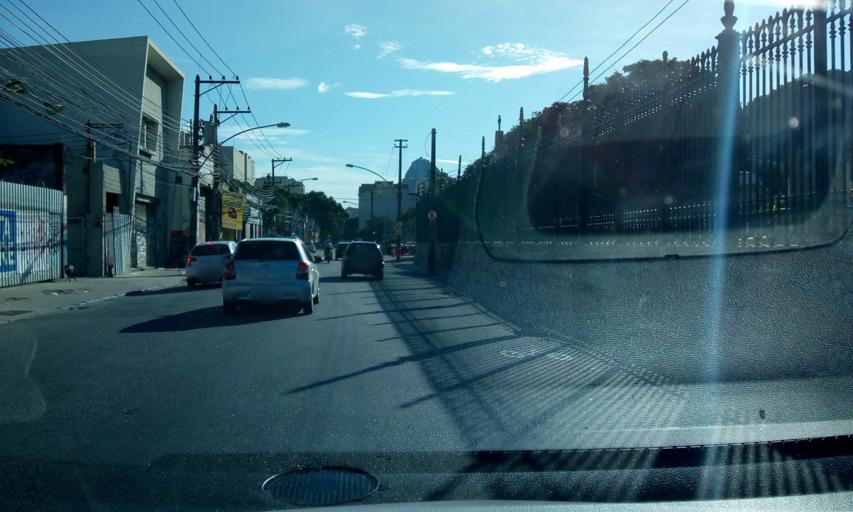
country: BR
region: Rio de Janeiro
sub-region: Rio De Janeiro
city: Rio de Janeiro
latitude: -22.9577
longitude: -43.1901
